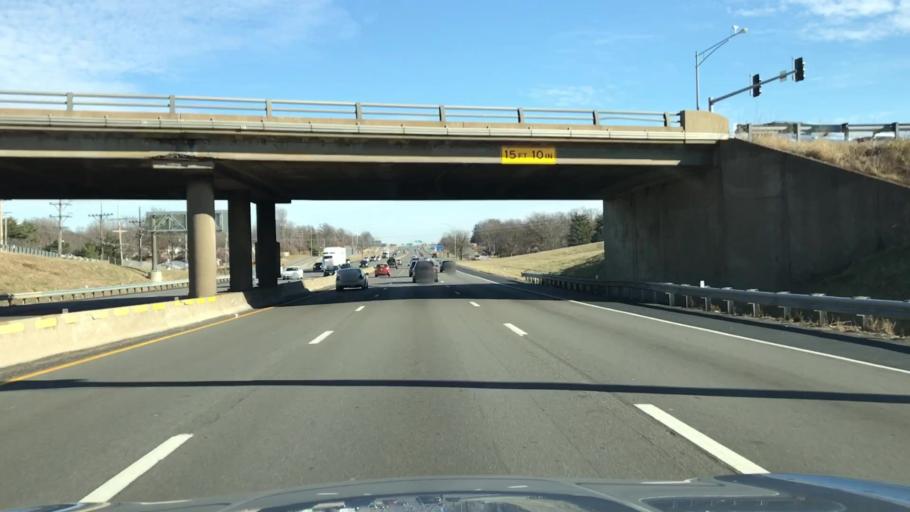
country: US
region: Missouri
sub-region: Saint Louis County
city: Castle Point
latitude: 38.7709
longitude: -90.2609
